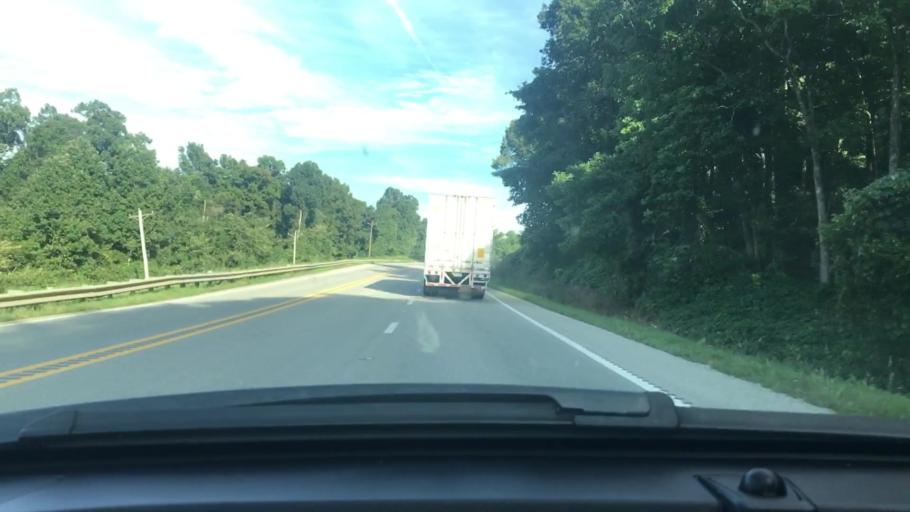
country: US
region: Arkansas
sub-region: Sharp County
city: Cherokee Village
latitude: 36.3005
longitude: -91.4090
